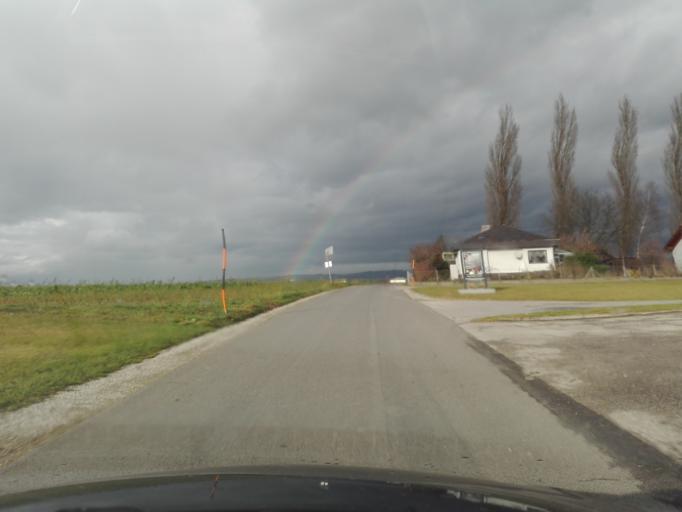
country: AT
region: Lower Austria
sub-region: Politischer Bezirk Amstetten
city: Strengberg
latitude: 48.1849
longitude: 14.6783
